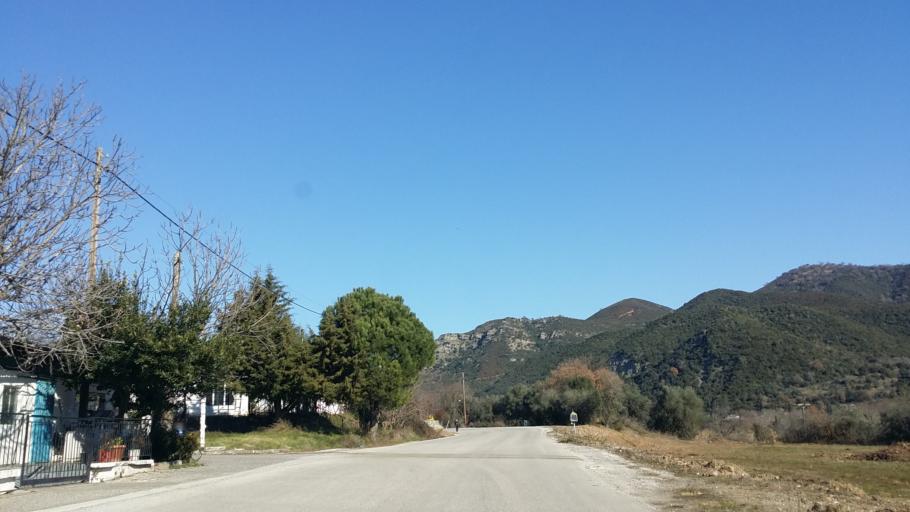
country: GR
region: West Greece
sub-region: Nomos Aitolias kai Akarnanias
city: Sardinia
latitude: 38.8897
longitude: 21.3465
